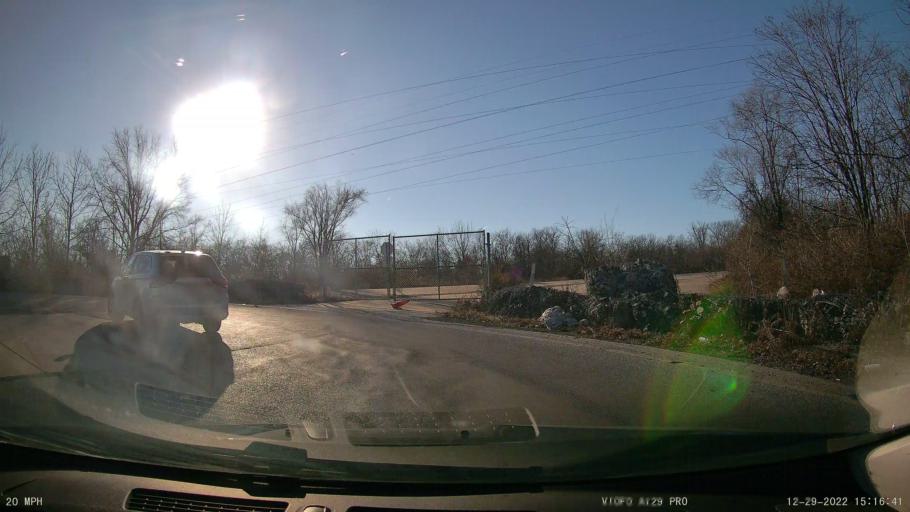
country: US
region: Pennsylvania
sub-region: Montgomery County
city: Bridgeport
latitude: 40.1059
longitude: -75.3535
